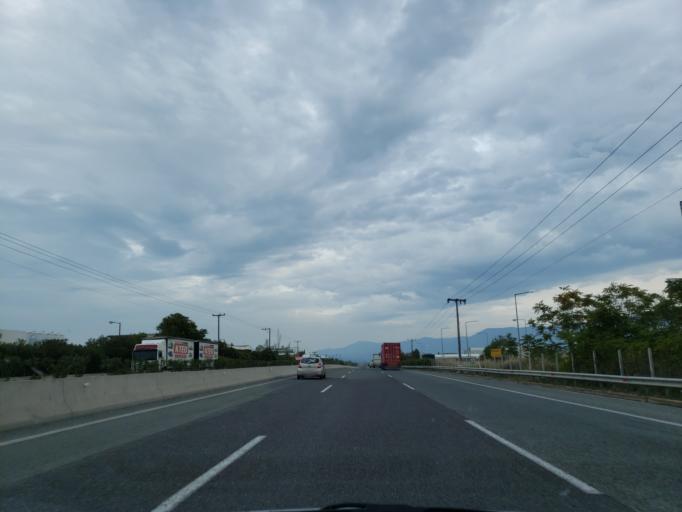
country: GR
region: Central Greece
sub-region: Nomos Voiotias
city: Oinofyta
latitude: 38.3236
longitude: 23.6162
